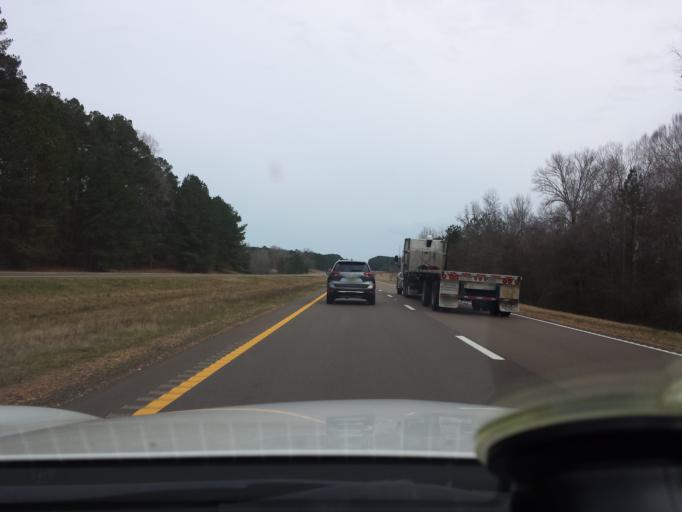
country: US
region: Mississippi
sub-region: Leake County
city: Carthage
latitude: 32.7570
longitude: -89.5850
